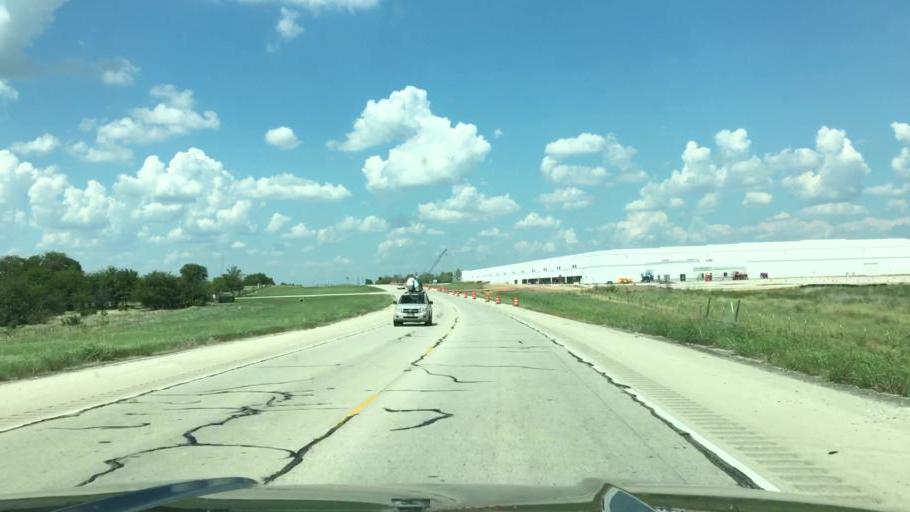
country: US
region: Texas
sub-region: Tarrant County
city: Haslet
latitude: 32.9822
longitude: -97.3420
